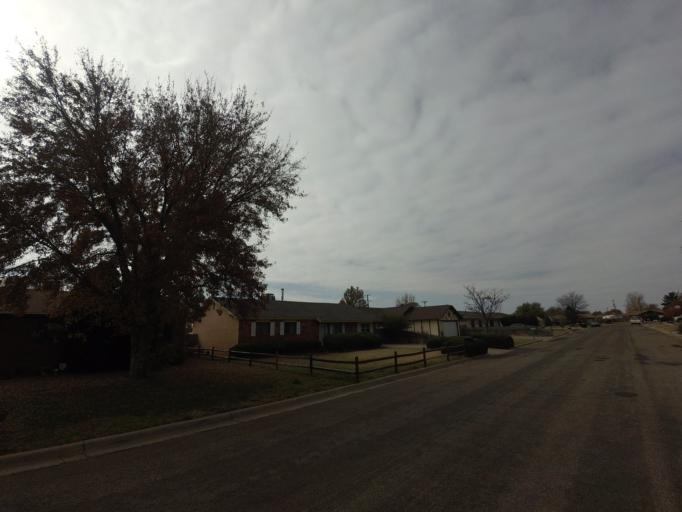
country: US
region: New Mexico
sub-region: Curry County
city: Clovis
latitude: 34.4313
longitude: -103.2157
